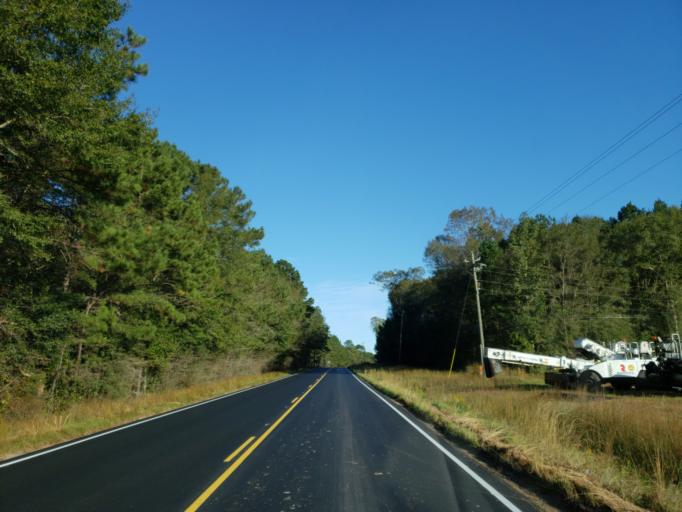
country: US
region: Mississippi
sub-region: Perry County
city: Richton
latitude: 31.3733
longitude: -88.8285
